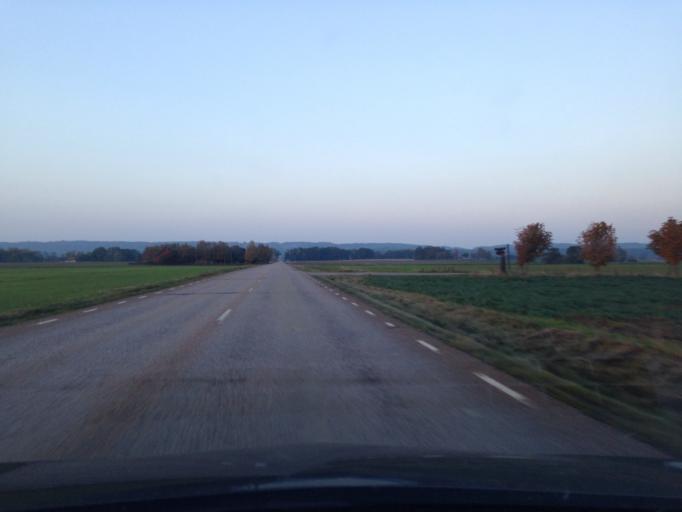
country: SE
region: Skane
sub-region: Angelholms Kommun
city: AEngelholm
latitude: 56.3096
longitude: 12.8849
